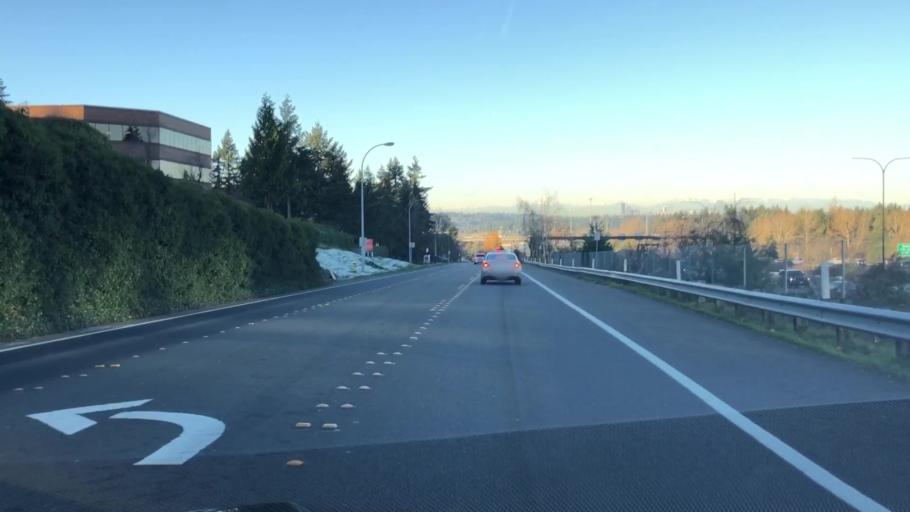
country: US
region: Washington
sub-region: King County
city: Eastgate
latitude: 47.5794
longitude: -122.1579
